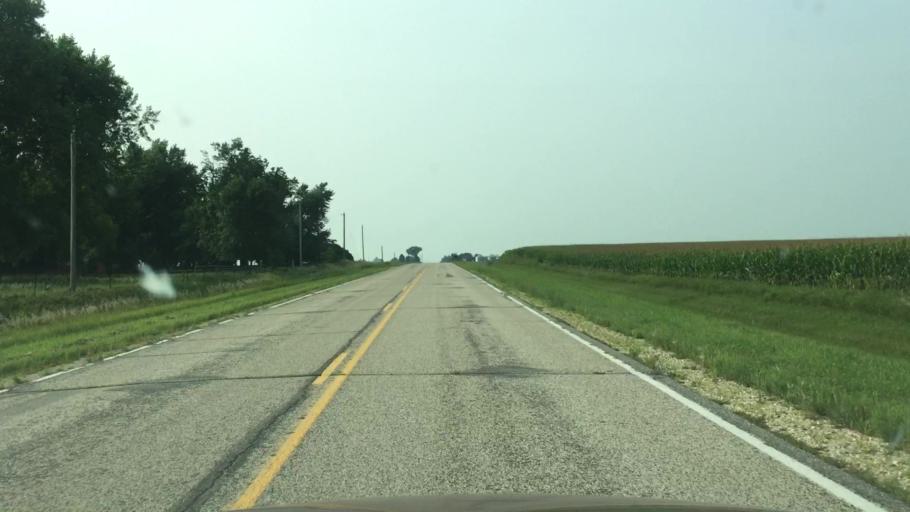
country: US
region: Iowa
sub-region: O'Brien County
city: Sheldon
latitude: 43.2783
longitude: -95.7829
